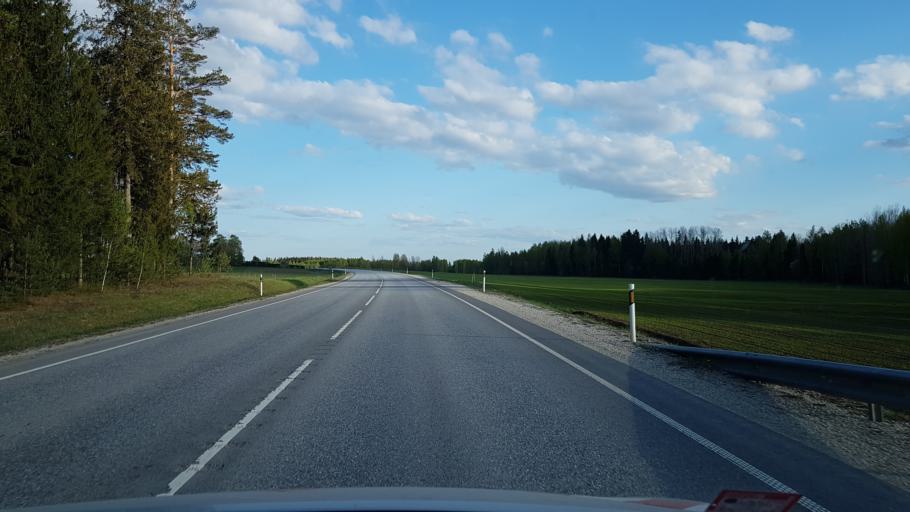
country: EE
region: Vorumaa
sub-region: Voru linn
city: Voru
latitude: 57.9283
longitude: 26.7998
